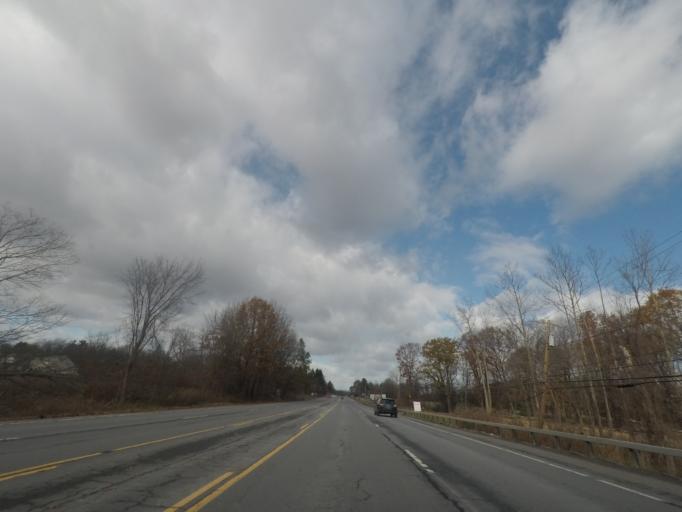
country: US
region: New York
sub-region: Saratoga County
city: Ballston Spa
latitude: 42.9863
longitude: -73.7871
